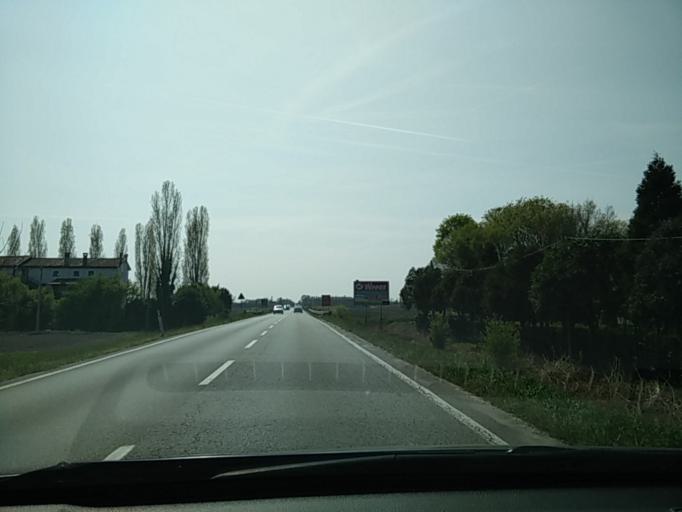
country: IT
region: Veneto
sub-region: Provincia di Venezia
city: Ceggia
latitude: 45.6652
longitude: 12.6165
